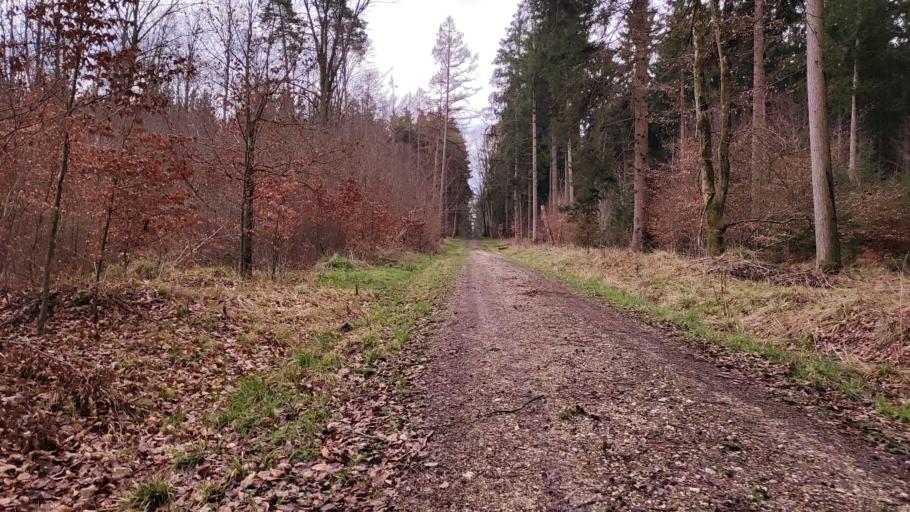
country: DE
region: Bavaria
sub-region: Swabia
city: Landensberg
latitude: 48.4318
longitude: 10.5566
